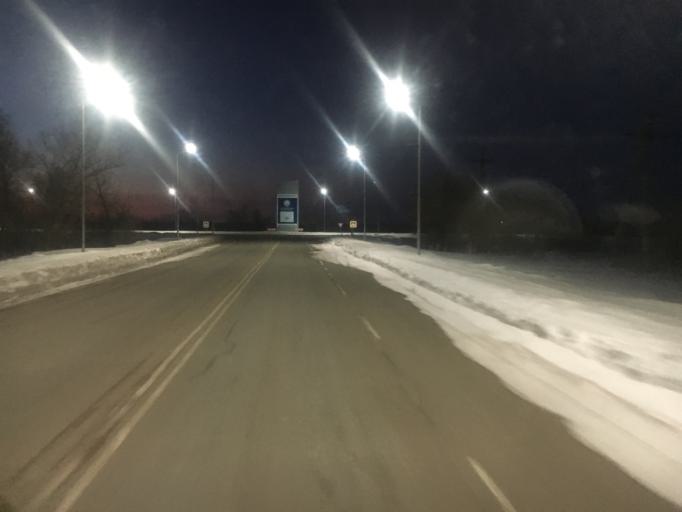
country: KZ
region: Batys Qazaqstan
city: Oral
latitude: 51.1646
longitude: 51.5249
